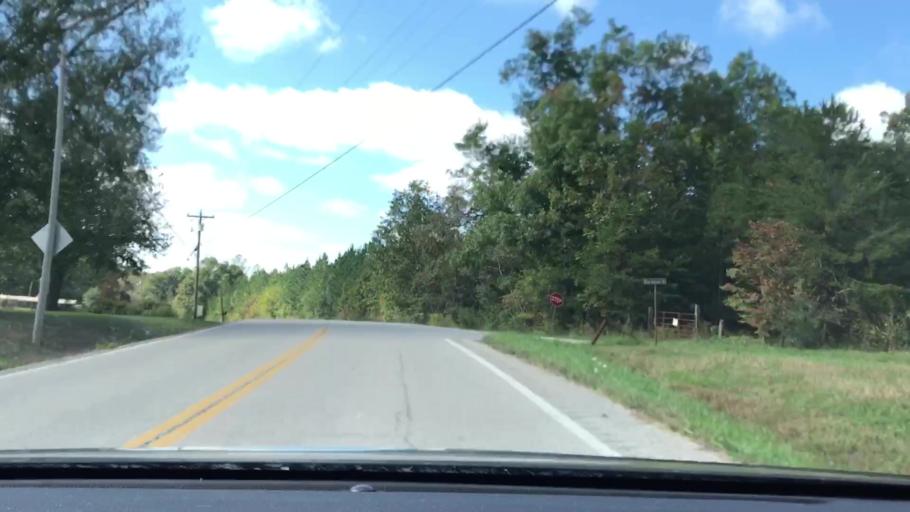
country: US
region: Tennessee
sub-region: Scott County
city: Huntsville
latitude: 36.3466
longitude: -84.6562
